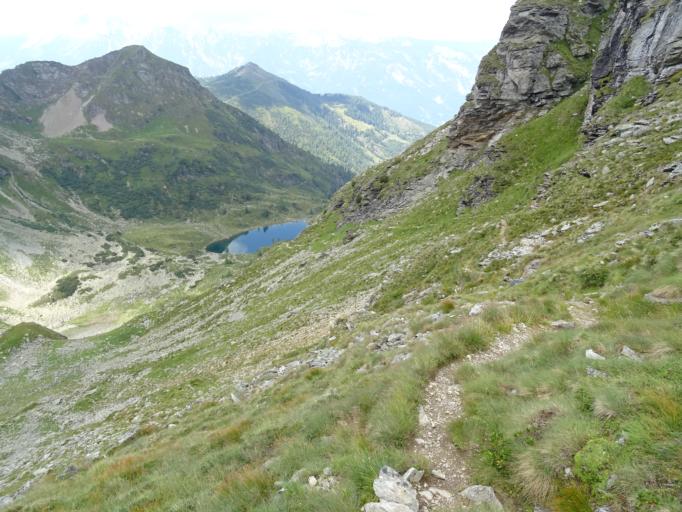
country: AT
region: Styria
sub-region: Politischer Bezirk Liezen
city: Haus
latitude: 47.3508
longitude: 13.7973
